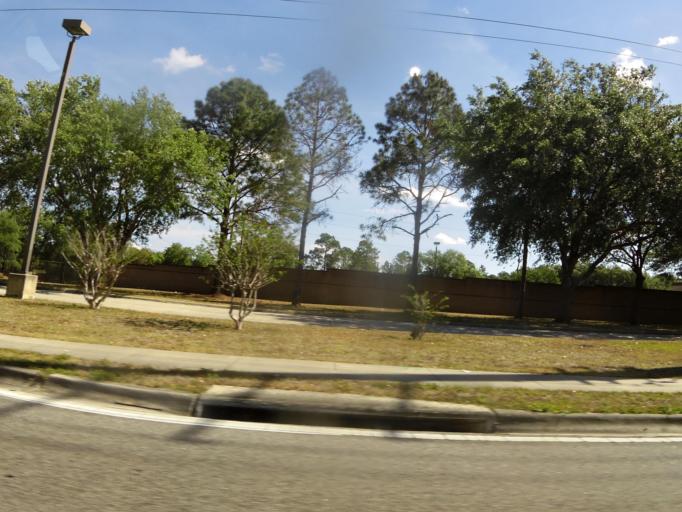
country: US
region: Florida
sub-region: Volusia County
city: Lake Helen
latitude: 28.9220
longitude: -81.1865
